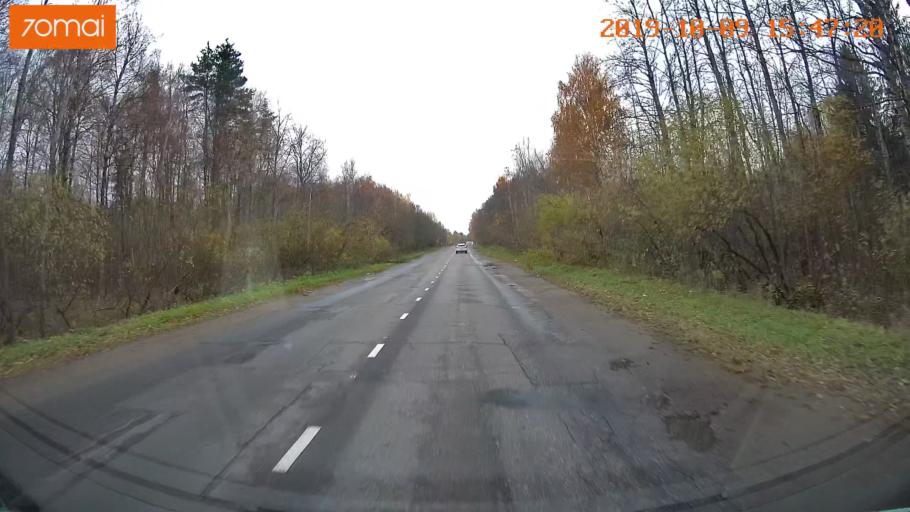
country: RU
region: Kostroma
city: Oktyabr'skiy
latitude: 57.8181
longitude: 41.0300
